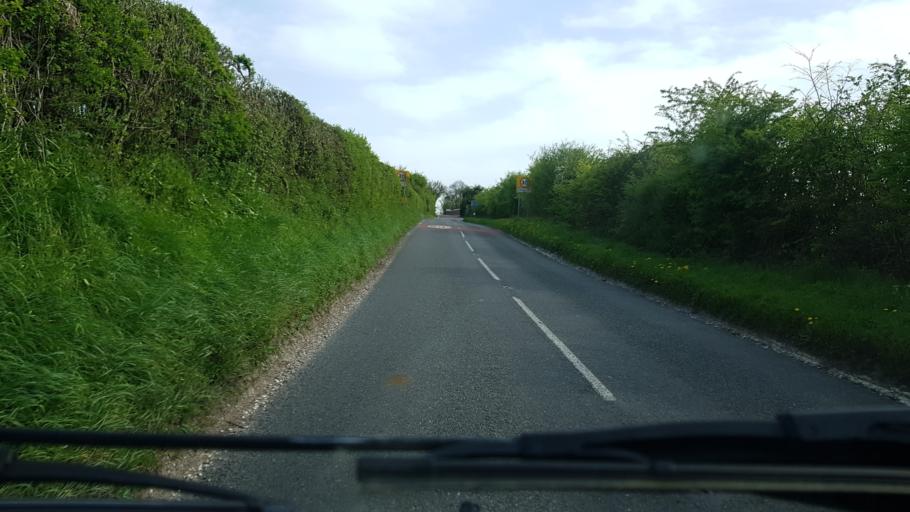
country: GB
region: England
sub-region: Hampshire
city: Overton
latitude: 51.2548
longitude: -1.2647
